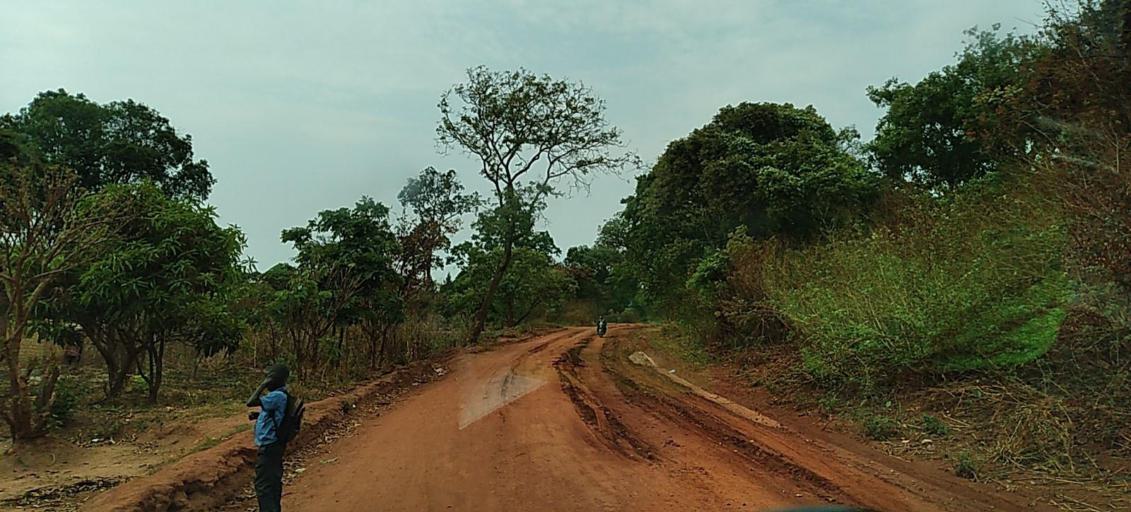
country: ZM
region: North-Western
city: Solwezi
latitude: -12.2456
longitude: 26.5125
